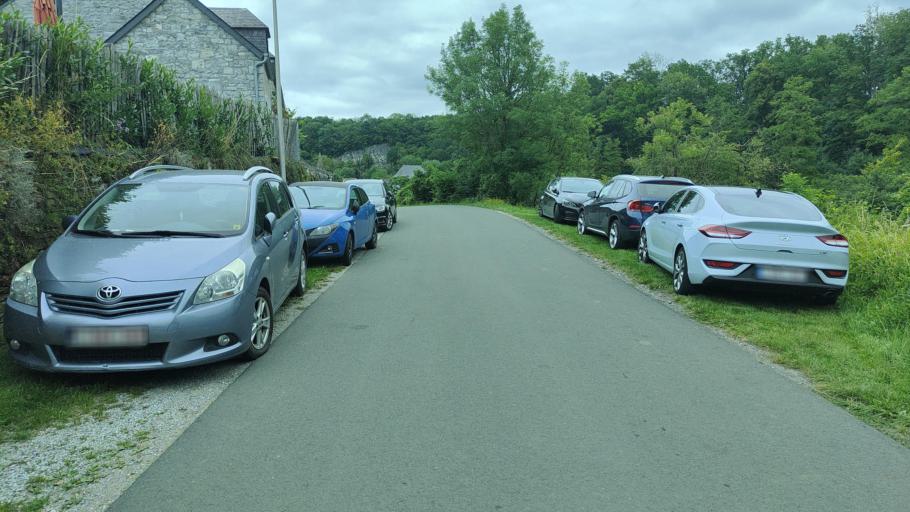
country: BE
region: Wallonia
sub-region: Province du Hainaut
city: Chimay
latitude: 50.0628
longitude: 4.3762
